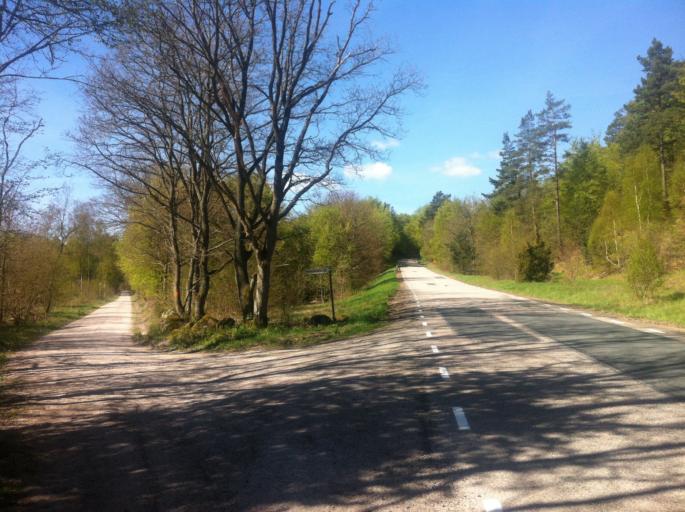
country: SE
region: Skane
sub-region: Kristianstads Kommun
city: Degeberga
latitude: 55.7279
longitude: 14.0665
